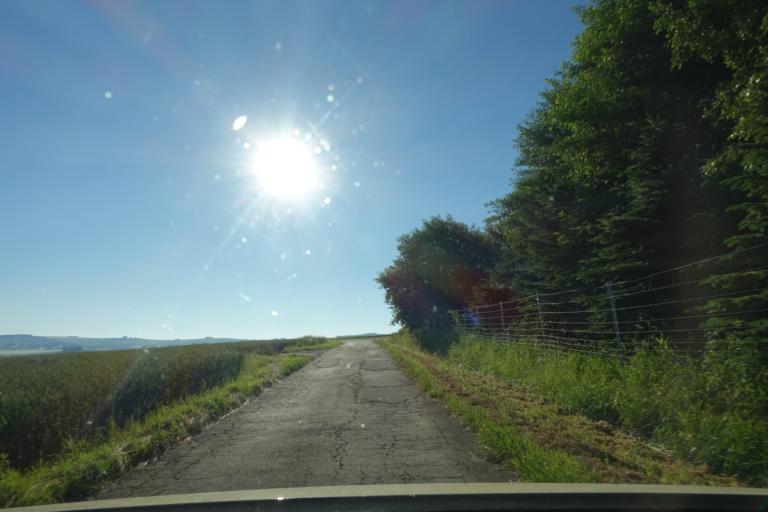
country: DE
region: Saxony
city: Eppendorf
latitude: 50.7787
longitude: 13.2428
